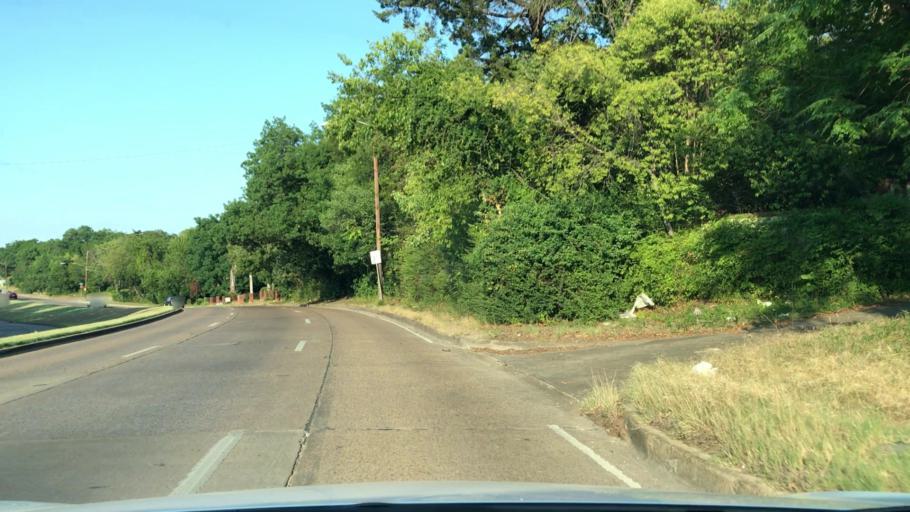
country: US
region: Texas
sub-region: Dallas County
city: Cockrell Hill
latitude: 32.7442
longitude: -96.8695
